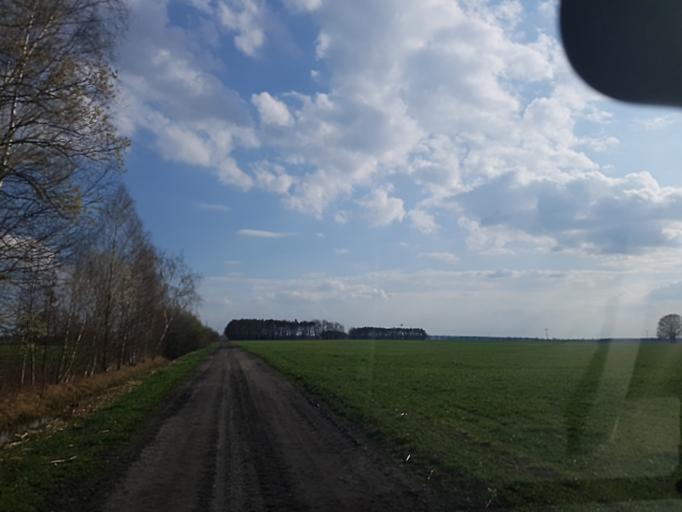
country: DE
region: Brandenburg
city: Schonborn
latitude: 51.6080
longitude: 13.5265
